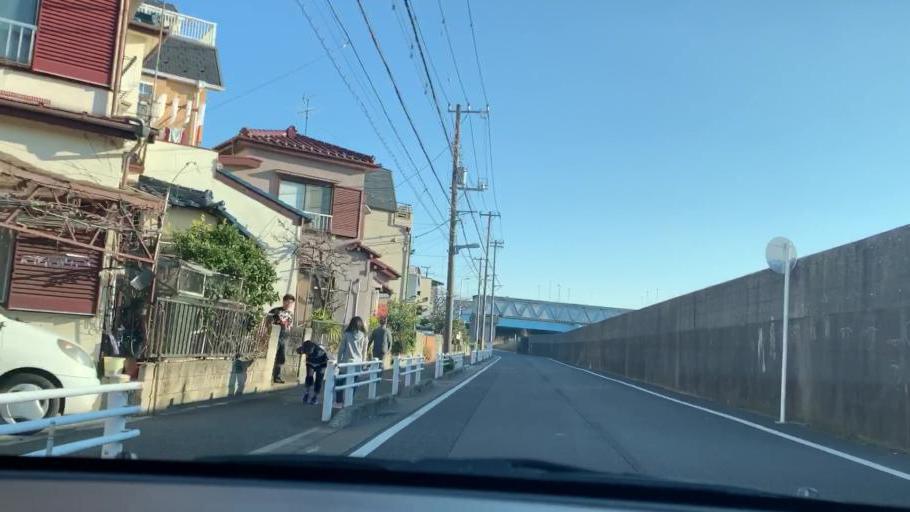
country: JP
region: Tokyo
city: Urayasu
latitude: 35.6407
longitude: 139.8875
